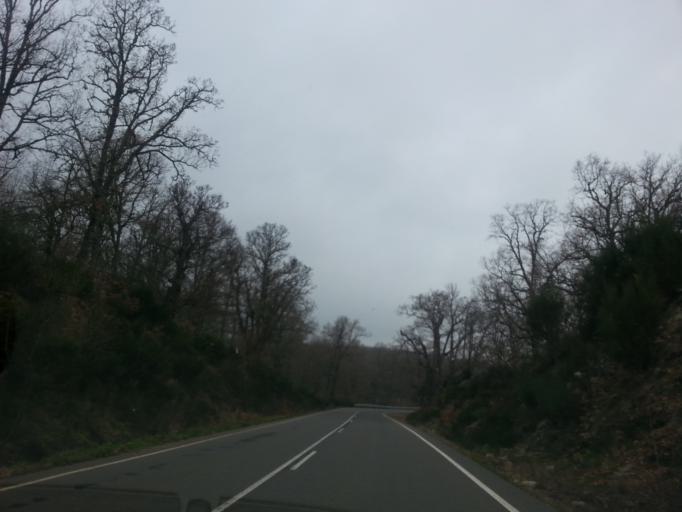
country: ES
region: Castille and Leon
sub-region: Provincia de Salamanca
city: La Alberca
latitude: 40.4837
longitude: -6.0853
